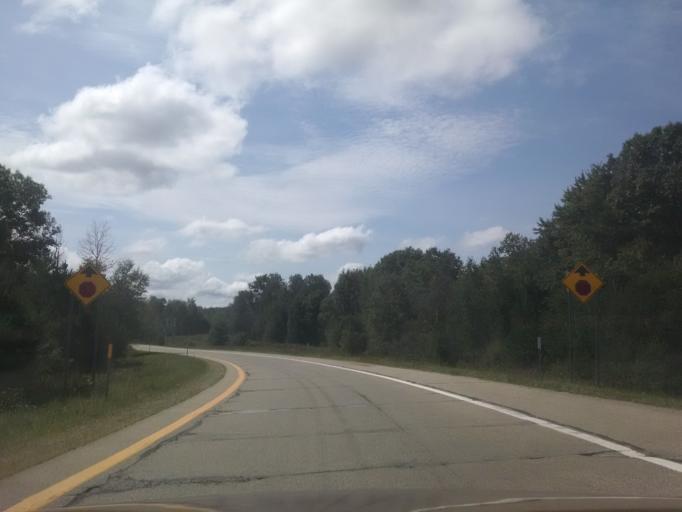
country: US
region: Michigan
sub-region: Clare County
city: Clare
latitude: 43.8671
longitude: -84.9101
